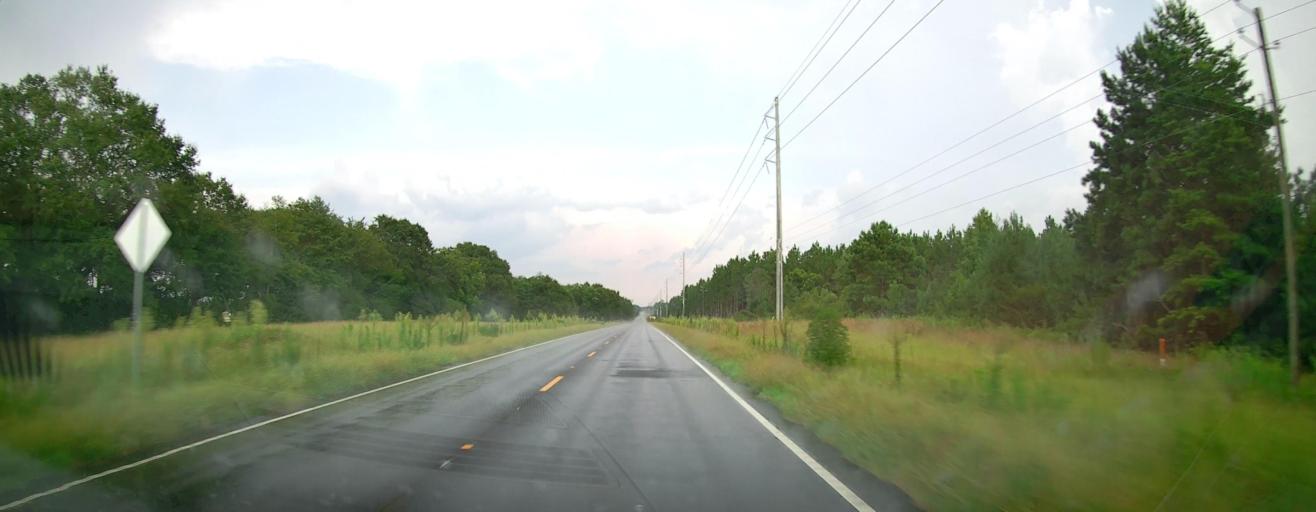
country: US
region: Georgia
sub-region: Dodge County
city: Chester
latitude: 32.5698
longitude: -83.1862
